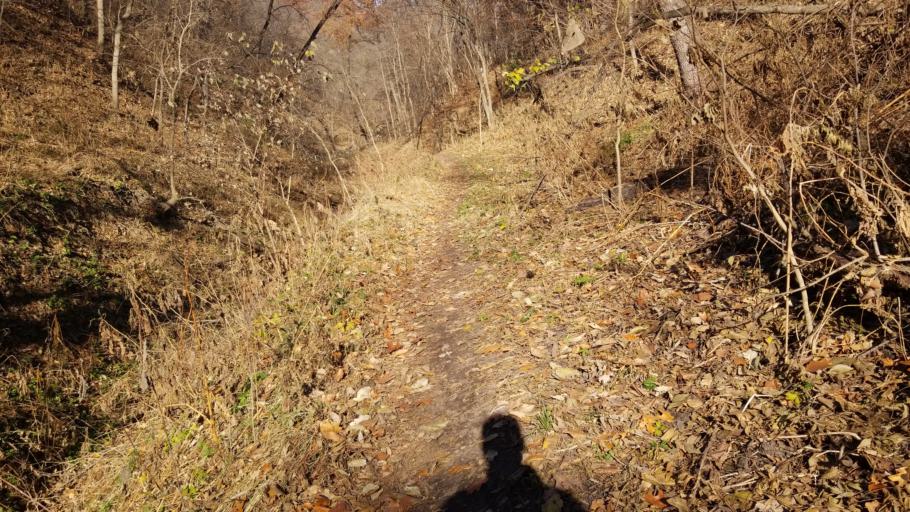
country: US
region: Nebraska
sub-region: Sarpy County
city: Bellevue
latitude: 41.1659
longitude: -95.8940
